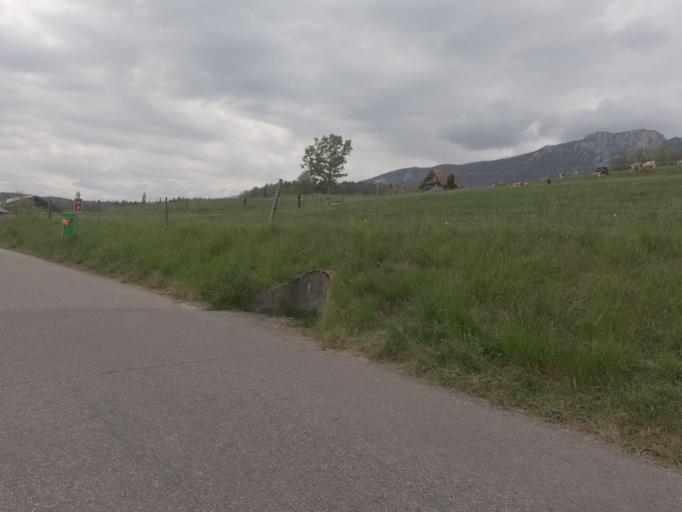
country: CH
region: Solothurn
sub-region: Bezirk Lebern
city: Riedholz
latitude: 47.2364
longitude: 7.5661
